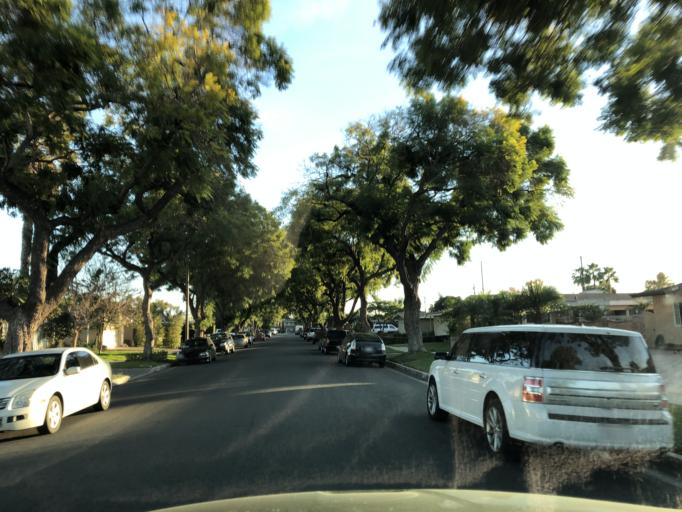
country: US
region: California
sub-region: Orange County
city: Tustin
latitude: 33.7551
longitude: -117.8457
